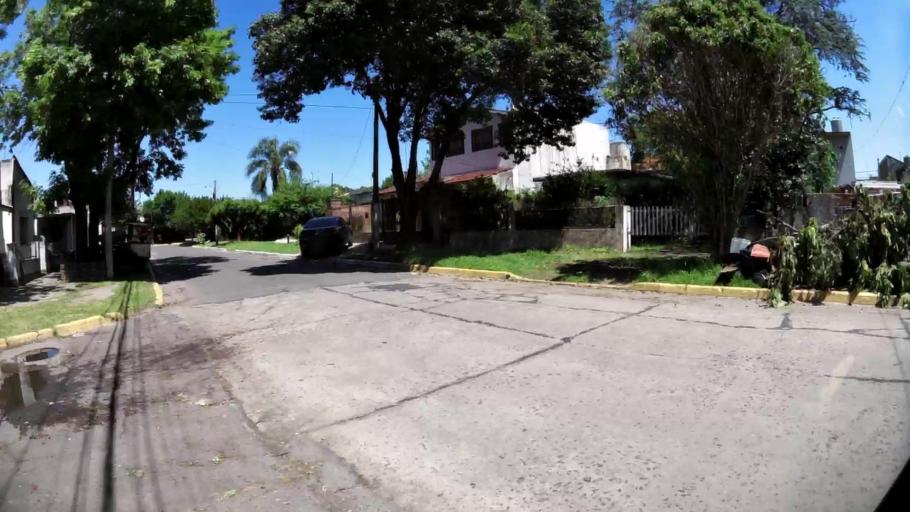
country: AR
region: Buenos Aires
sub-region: Partido de Merlo
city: Merlo
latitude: -34.6751
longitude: -58.6902
